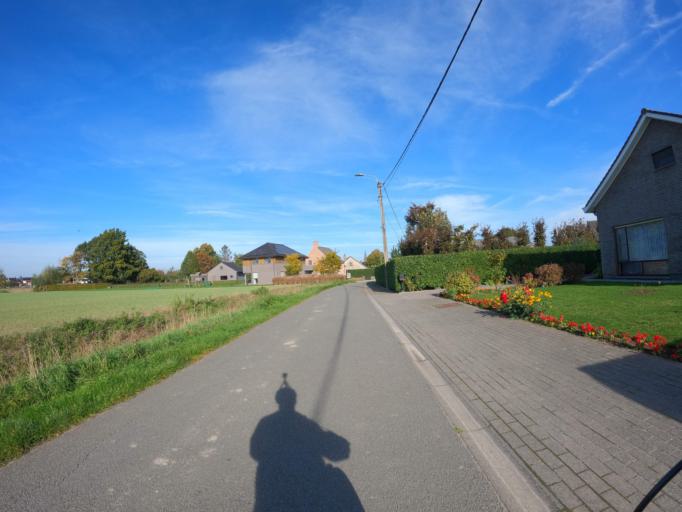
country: BE
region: Flanders
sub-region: Provincie West-Vlaanderen
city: Ruiselede
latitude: 51.0363
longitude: 3.3909
